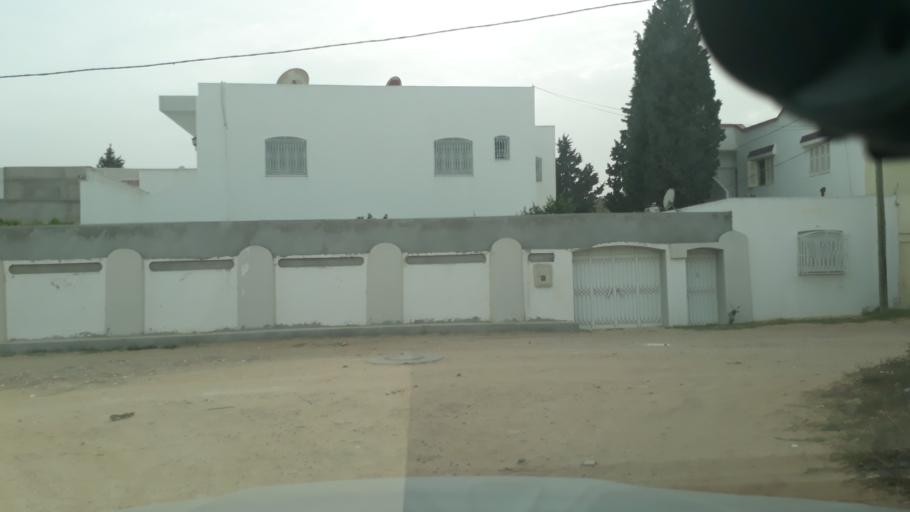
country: TN
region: Safaqis
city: Al Qarmadah
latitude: 34.7811
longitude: 10.7667
